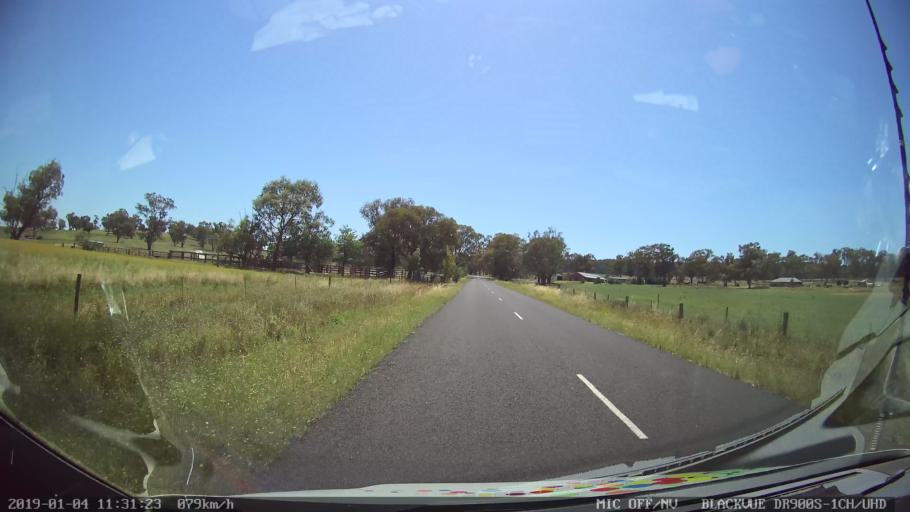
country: AU
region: New South Wales
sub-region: Cabonne
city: Molong
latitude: -33.0726
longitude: 148.7930
